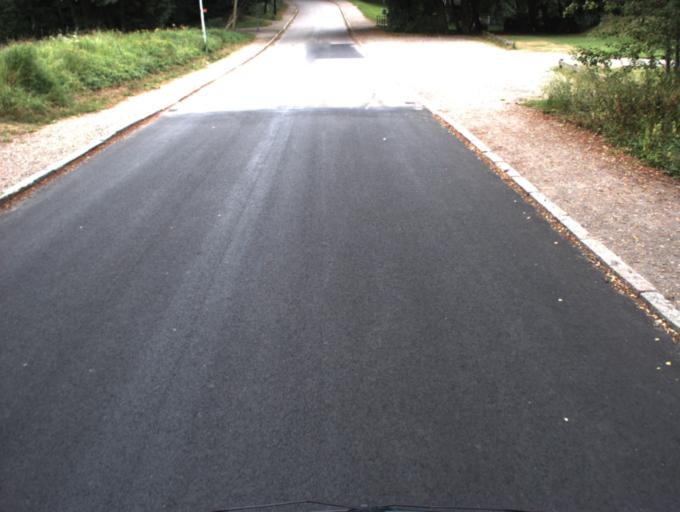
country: SE
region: Skane
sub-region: Helsingborg
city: Helsingborg
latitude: 56.0362
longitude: 12.7287
